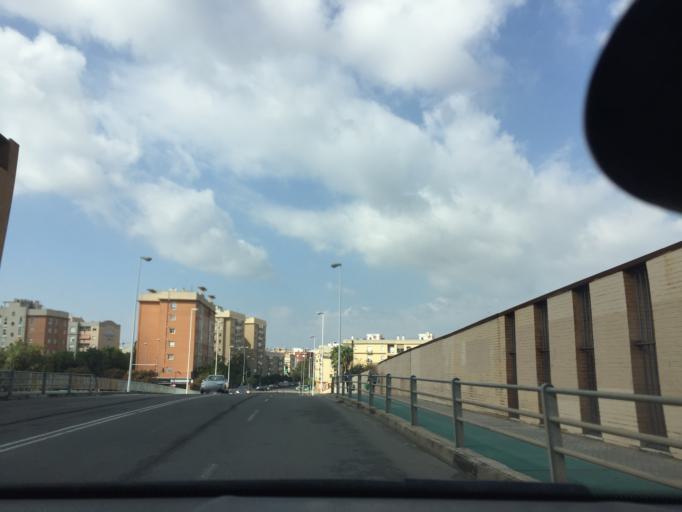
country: ES
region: Andalusia
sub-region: Provincia de Sevilla
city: Sevilla
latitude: 37.3945
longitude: -5.9725
